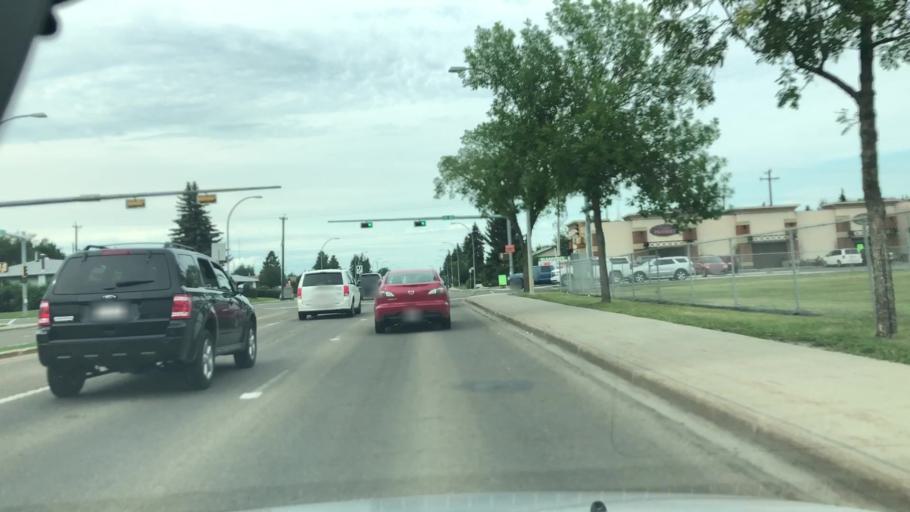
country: CA
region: Alberta
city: Edmonton
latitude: 53.5943
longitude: -113.5165
